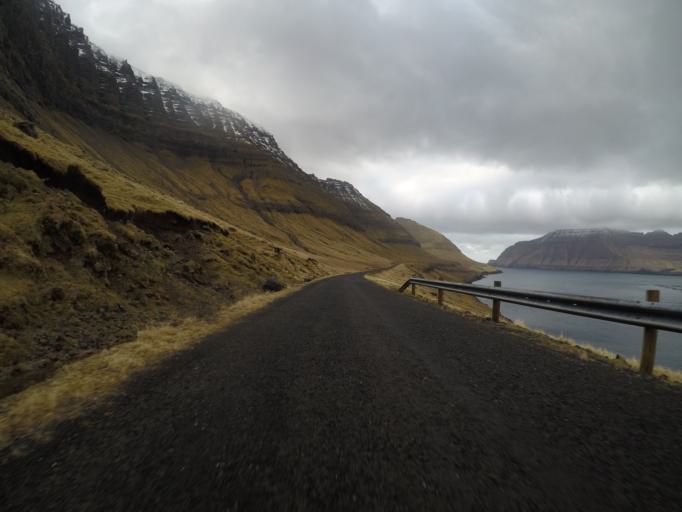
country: FO
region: Nordoyar
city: Klaksvik
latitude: 62.3304
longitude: -6.5726
